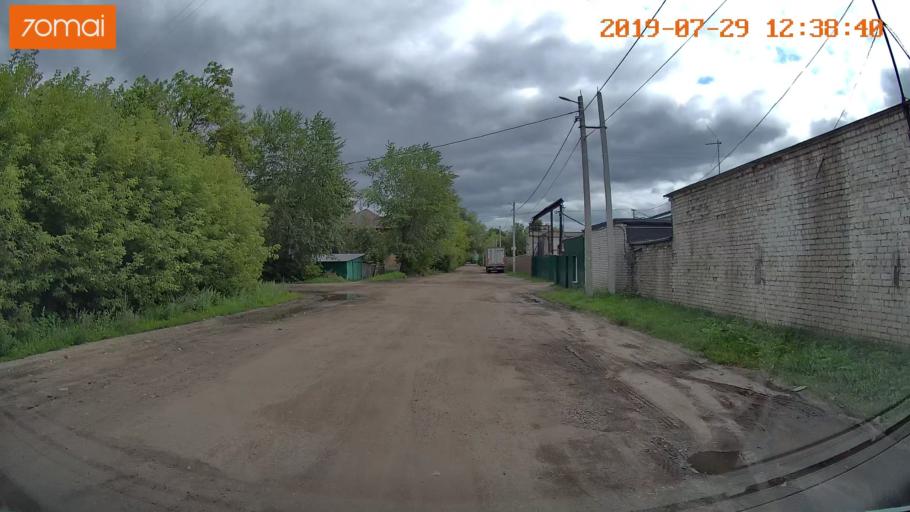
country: RU
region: Ivanovo
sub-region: Gorod Ivanovo
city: Ivanovo
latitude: 57.0052
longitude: 40.9416
